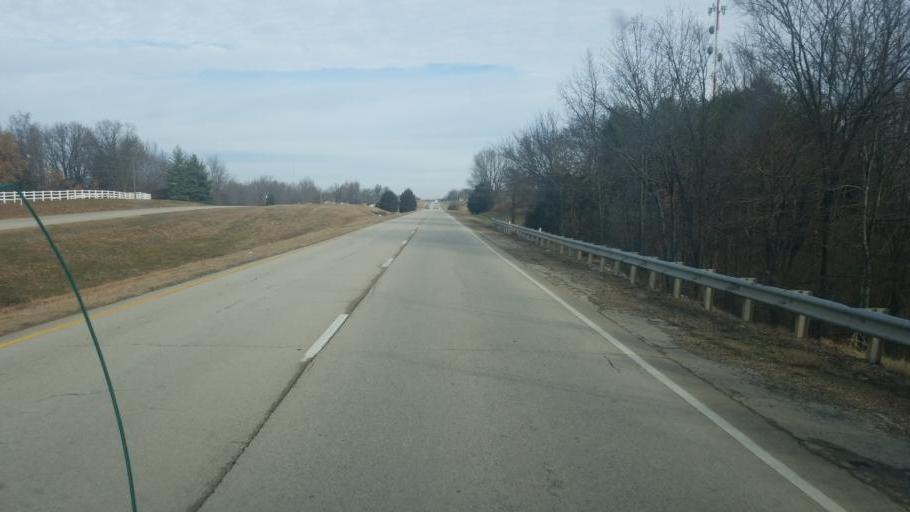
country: US
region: Missouri
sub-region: Stoddard County
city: Bloomfield
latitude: 36.8417
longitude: -89.9417
